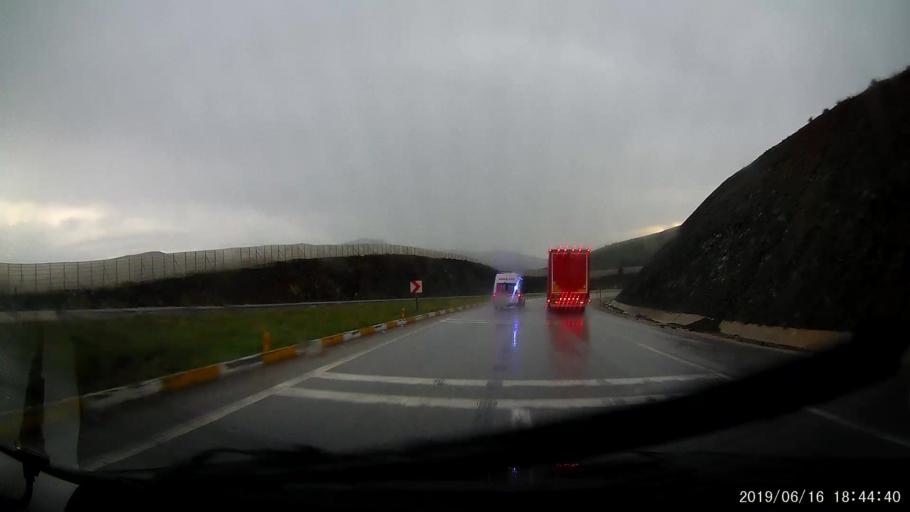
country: TR
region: Erzincan
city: Doganbeyli
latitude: 39.8695
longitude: 39.0682
